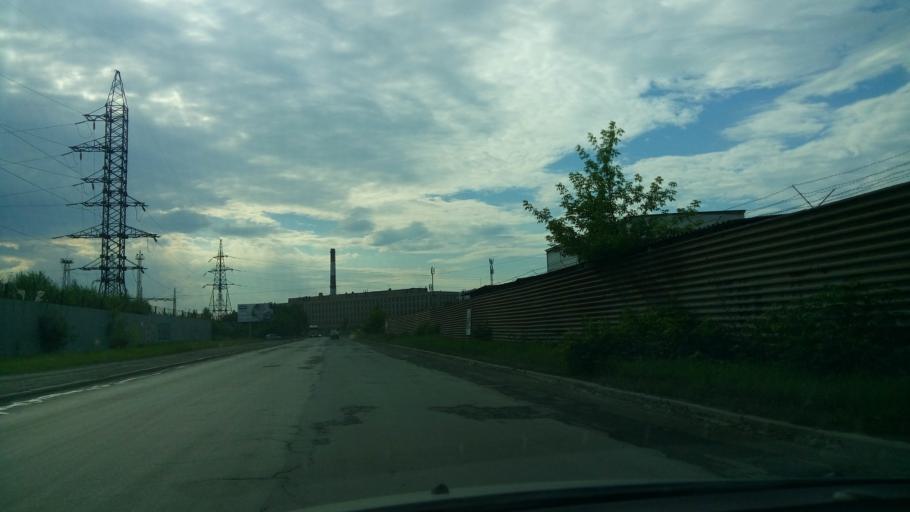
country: RU
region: Sverdlovsk
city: Yekaterinburg
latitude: 56.8870
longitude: 60.6577
